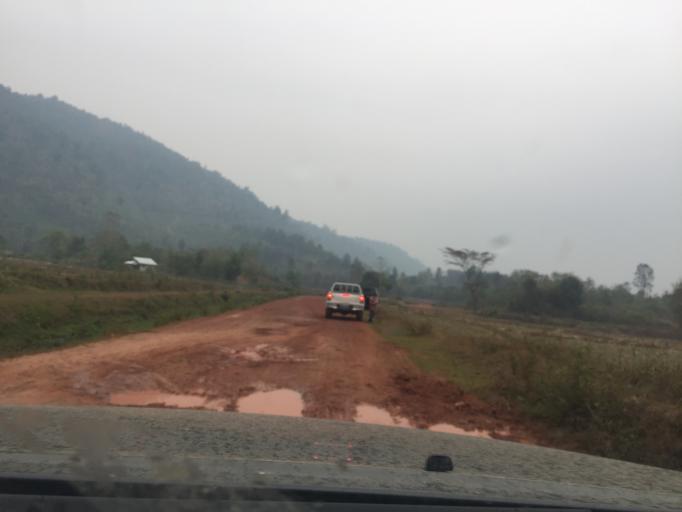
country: LA
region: Xiagnabouli
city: Sainyabuli
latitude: 18.9851
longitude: 101.4841
